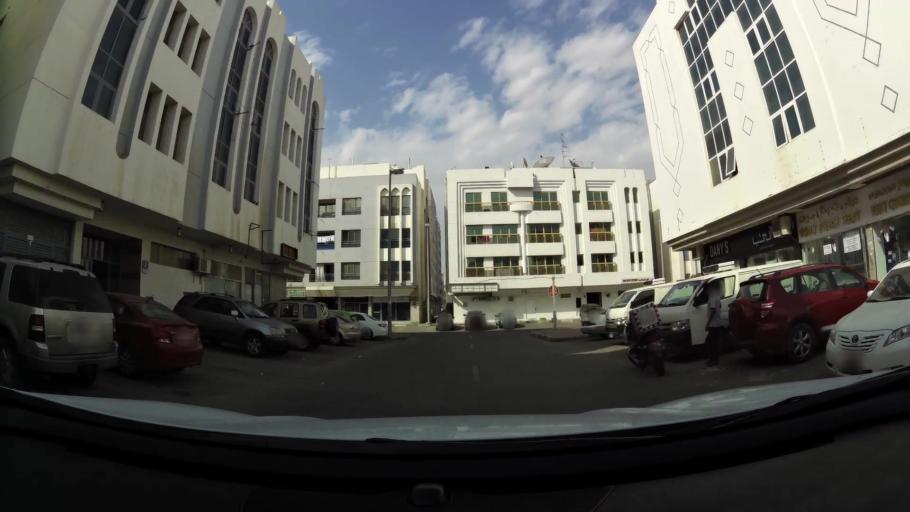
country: AE
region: Abu Dhabi
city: Abu Dhabi
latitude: 24.3279
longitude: 54.5341
